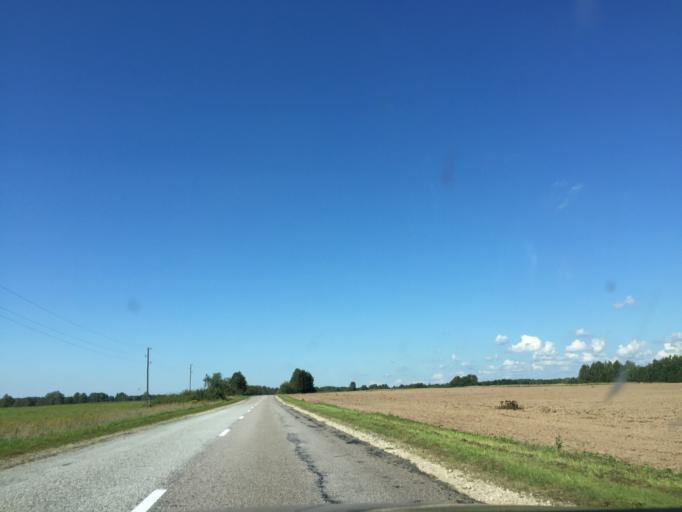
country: LV
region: Limbazu Rajons
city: Limbazi
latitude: 57.4567
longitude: 24.7217
